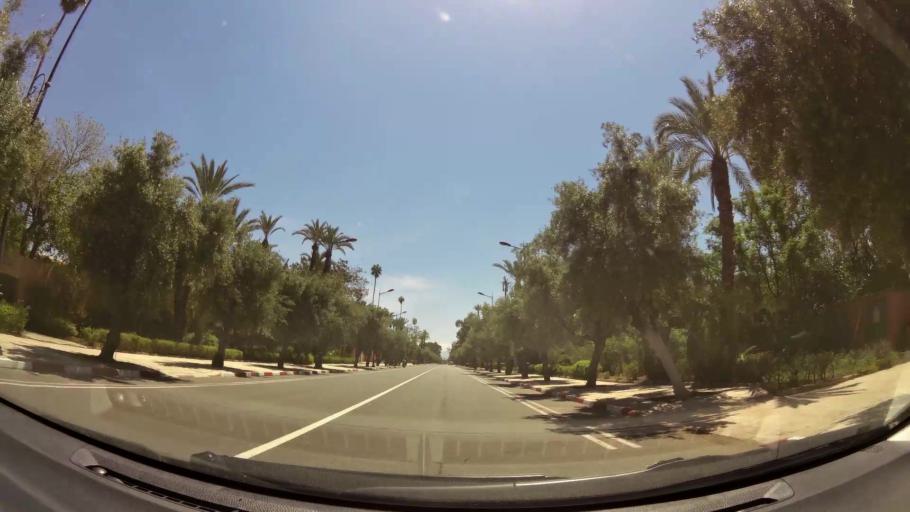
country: MA
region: Marrakech-Tensift-Al Haouz
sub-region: Marrakech
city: Marrakesh
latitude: 31.6268
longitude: -8.0108
